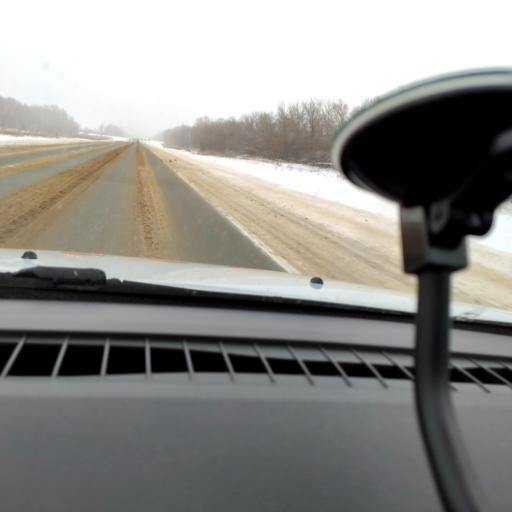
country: RU
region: Samara
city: Dubovyy Umet
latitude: 53.0359
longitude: 50.2133
